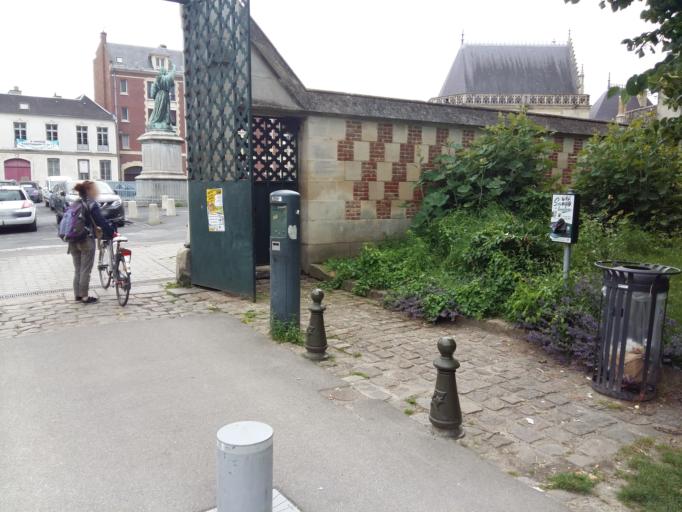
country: FR
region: Picardie
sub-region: Departement de la Somme
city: Amiens
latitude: 49.8942
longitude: 2.3035
